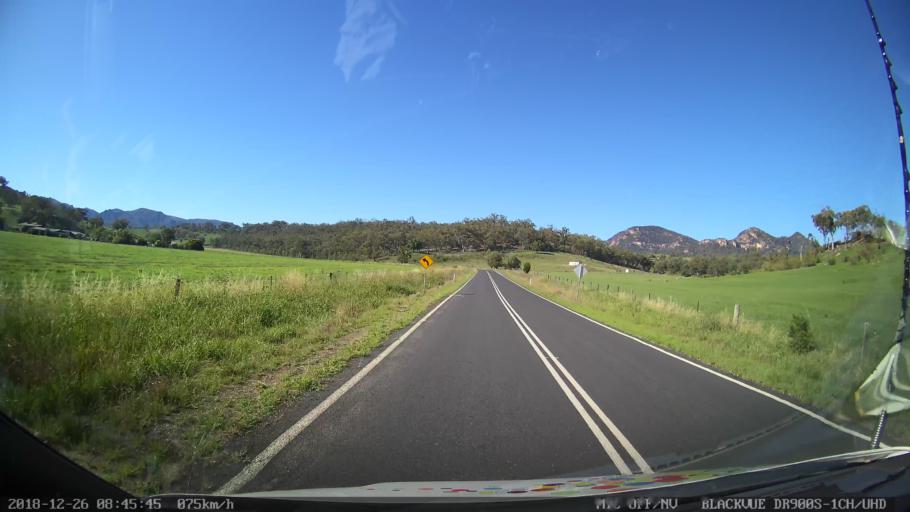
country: AU
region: New South Wales
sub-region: Mid-Western Regional
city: Kandos
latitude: -32.5287
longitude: 150.0864
